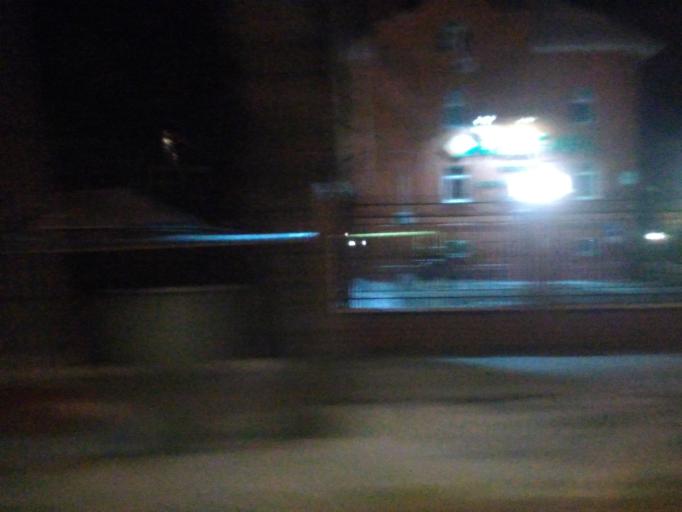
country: RU
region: Ulyanovsk
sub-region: Ulyanovskiy Rayon
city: Ulyanovsk
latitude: 54.3321
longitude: 48.4006
